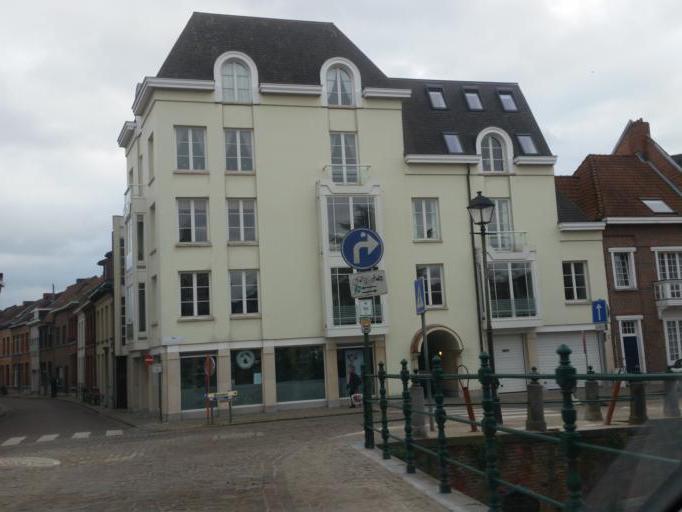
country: BE
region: Flanders
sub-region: Provincie Antwerpen
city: Lier
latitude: 51.1290
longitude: 4.5706
